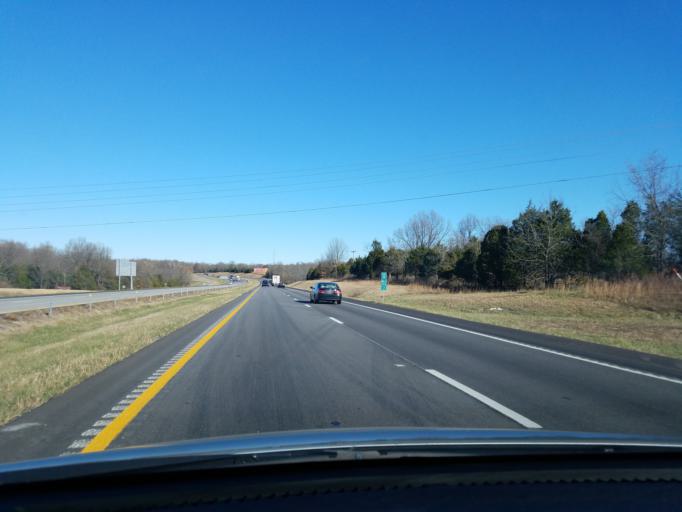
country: US
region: Missouri
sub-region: Webster County
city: Marshfield
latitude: 37.3548
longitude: -92.9156
